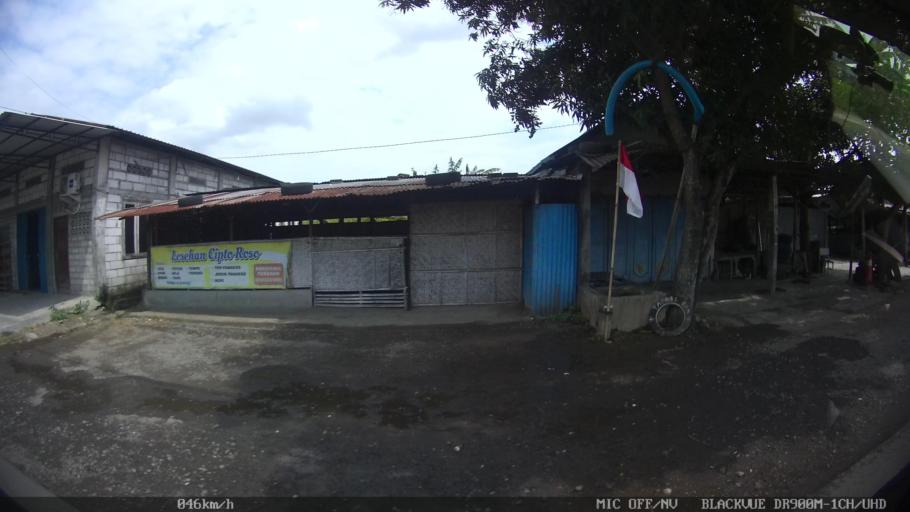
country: ID
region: Daerah Istimewa Yogyakarta
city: Depok
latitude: -7.8321
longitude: 110.4775
